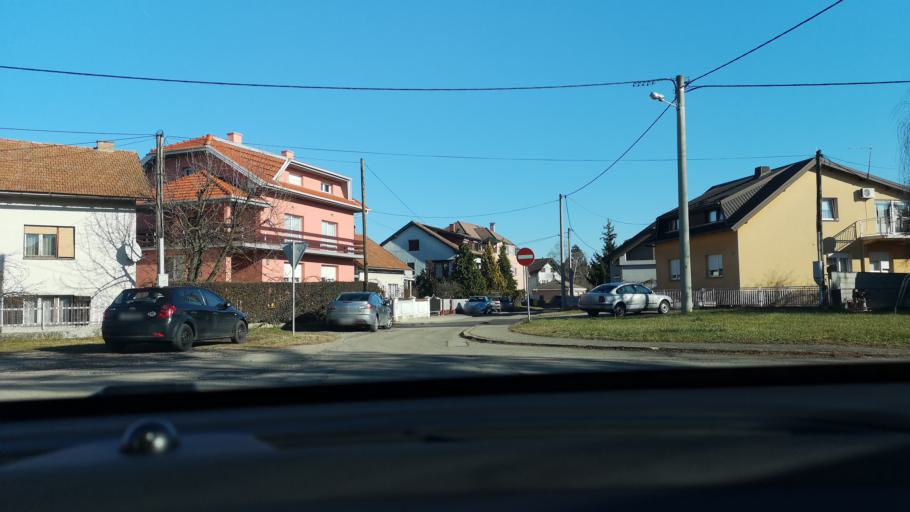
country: HR
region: Zagrebacka
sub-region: Grad Velika Gorica
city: Velika Gorica
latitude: 45.7206
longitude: 16.0647
